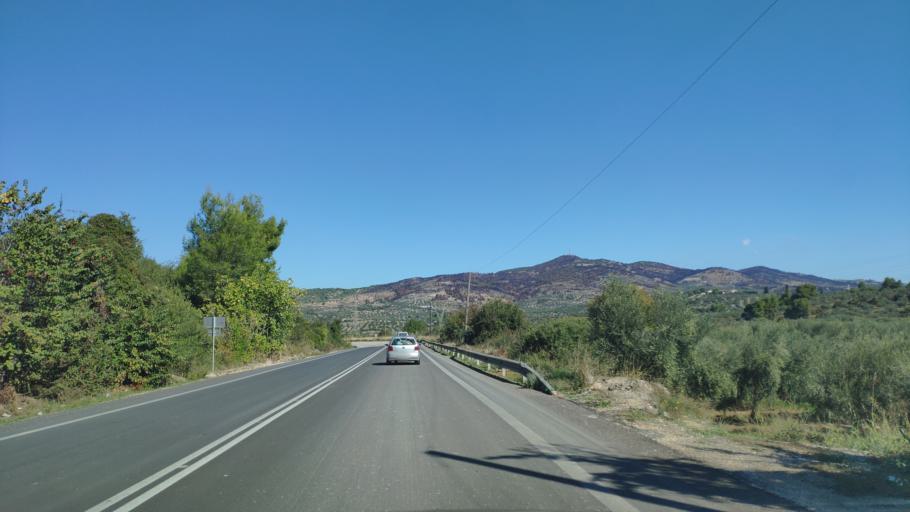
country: GR
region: Peloponnese
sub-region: Nomos Korinthias
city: Athikia
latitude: 37.8375
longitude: 22.8988
